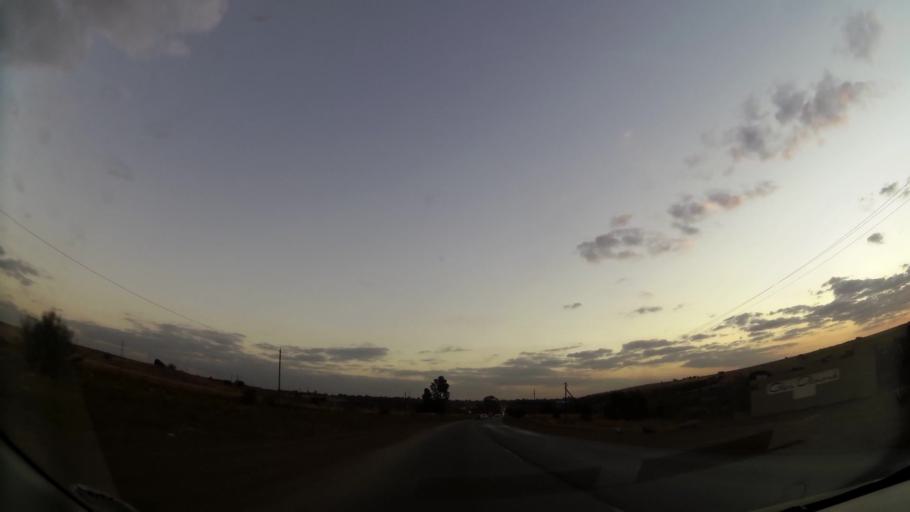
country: ZA
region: Gauteng
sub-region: West Rand District Municipality
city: Krugersdorp
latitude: -26.0599
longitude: 27.7019
